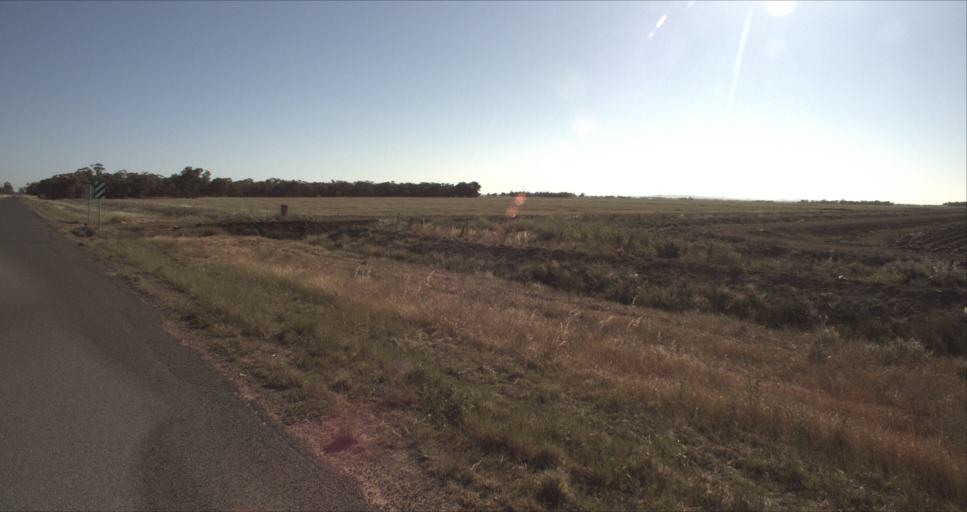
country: AU
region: New South Wales
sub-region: Leeton
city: Leeton
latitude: -34.5672
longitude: 146.2642
